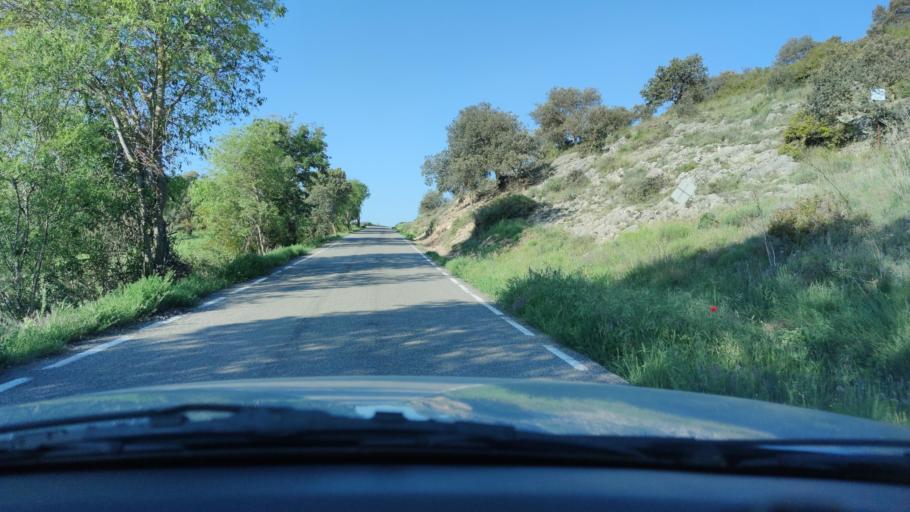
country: ES
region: Catalonia
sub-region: Provincia de Lleida
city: Artesa de Segre
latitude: 41.8808
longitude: 1.0185
